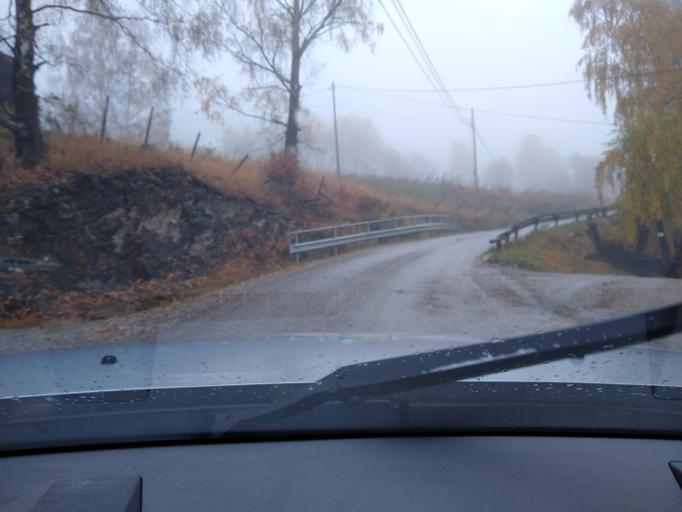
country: NO
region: Oppland
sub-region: Ringebu
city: Ringebu
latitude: 61.5298
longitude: 10.1532
